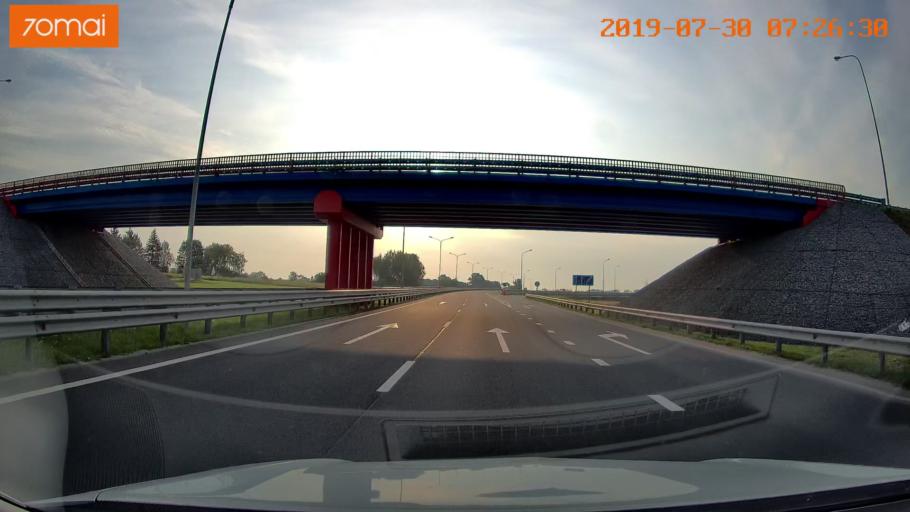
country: RU
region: Kaliningrad
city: Gvardeysk
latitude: 54.6834
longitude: 20.8633
